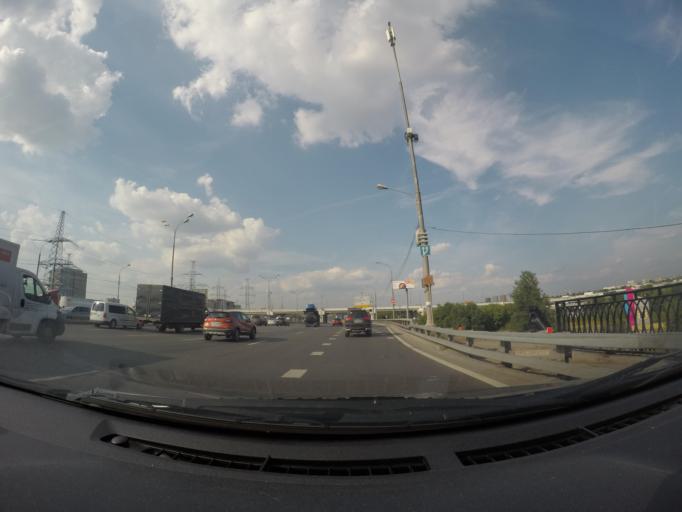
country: RU
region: Moscow
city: Zhulebino
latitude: 55.7100
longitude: 37.8365
